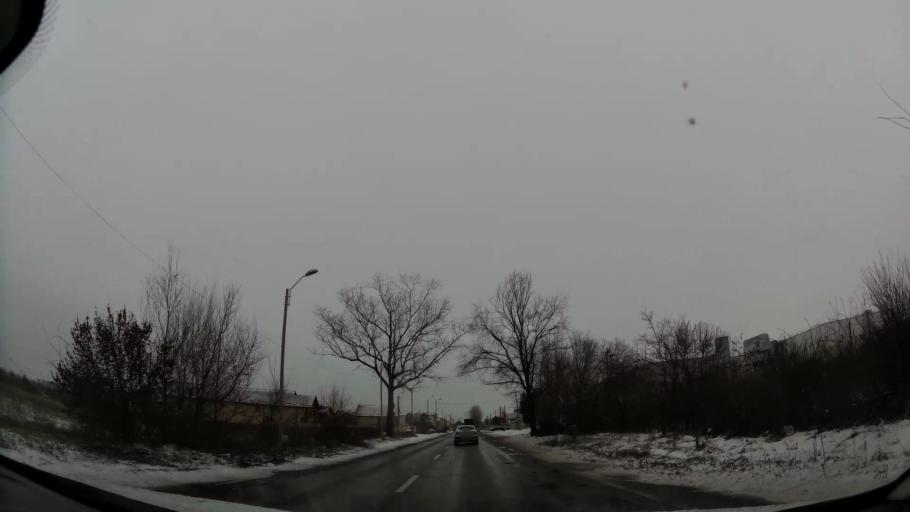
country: RO
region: Dambovita
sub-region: Comuna Ulmi
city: Ulmi
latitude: 44.9036
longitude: 25.4968
